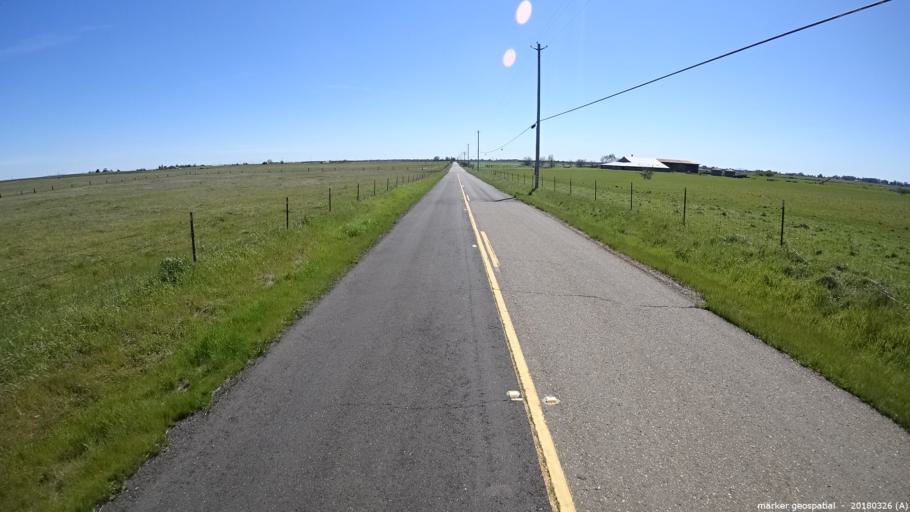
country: US
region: California
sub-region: Sacramento County
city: Wilton
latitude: 38.4791
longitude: -121.2607
